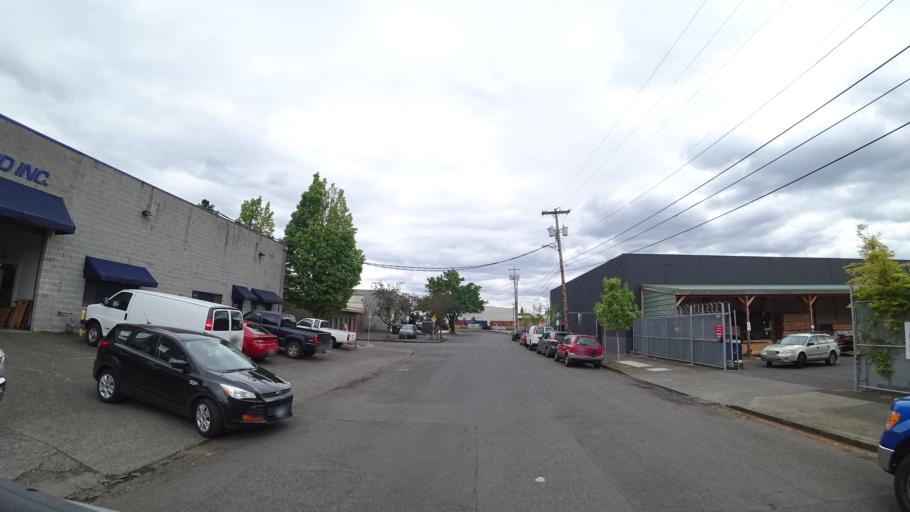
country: US
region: Oregon
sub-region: Multnomah County
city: Portland
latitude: 45.5031
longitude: -122.6517
